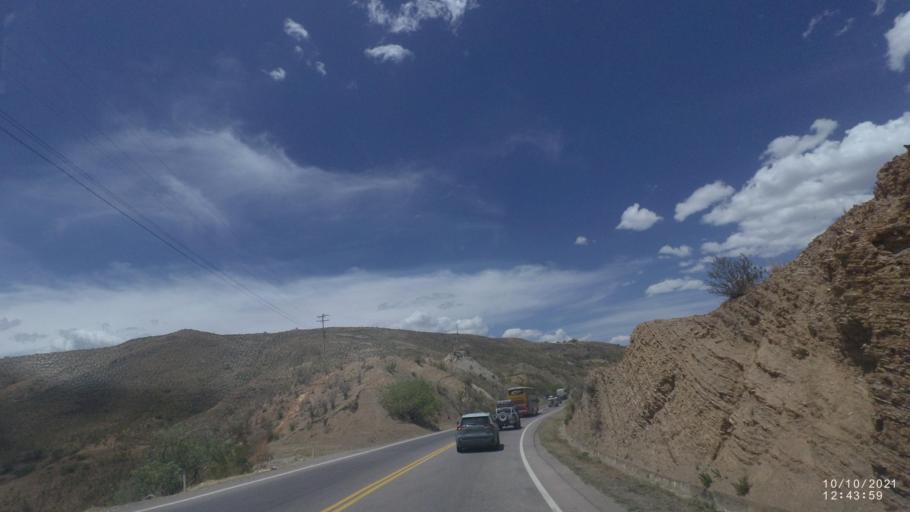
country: BO
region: Cochabamba
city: Irpa Irpa
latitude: -17.6297
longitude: -66.3810
